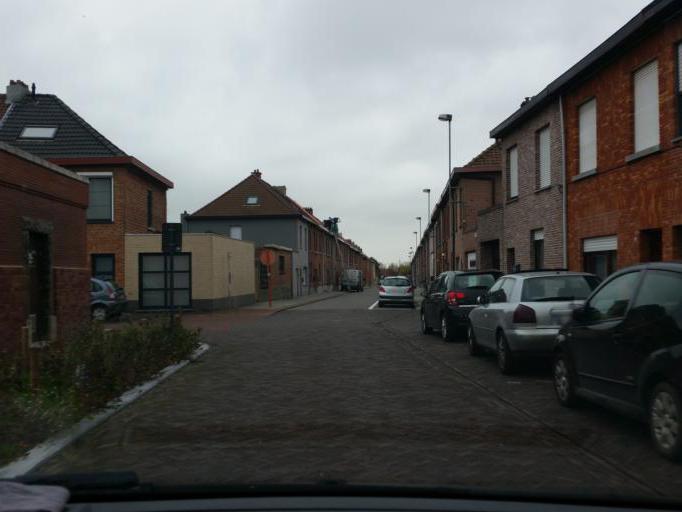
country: BE
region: Flanders
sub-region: Provincie Vlaams-Brabant
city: Machelen
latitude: 50.9124
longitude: 4.4447
